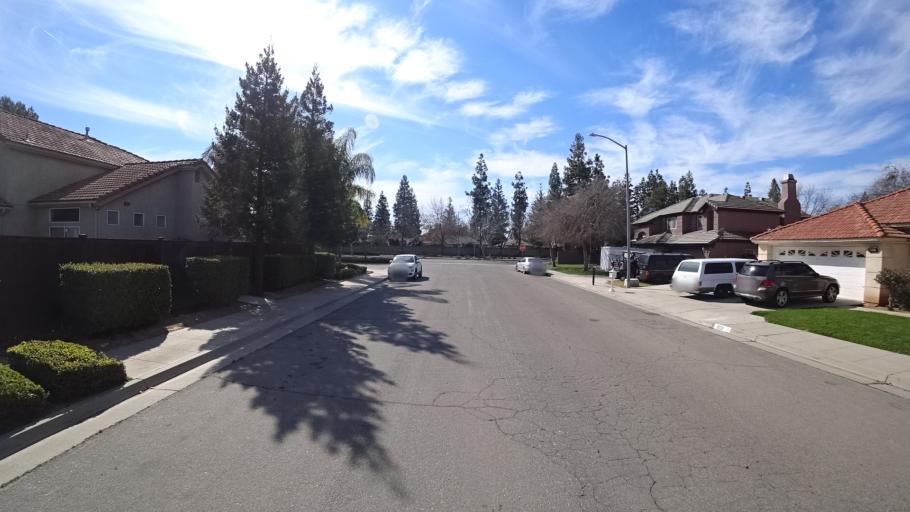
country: US
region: California
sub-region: Fresno County
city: Clovis
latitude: 36.8526
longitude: -119.7538
